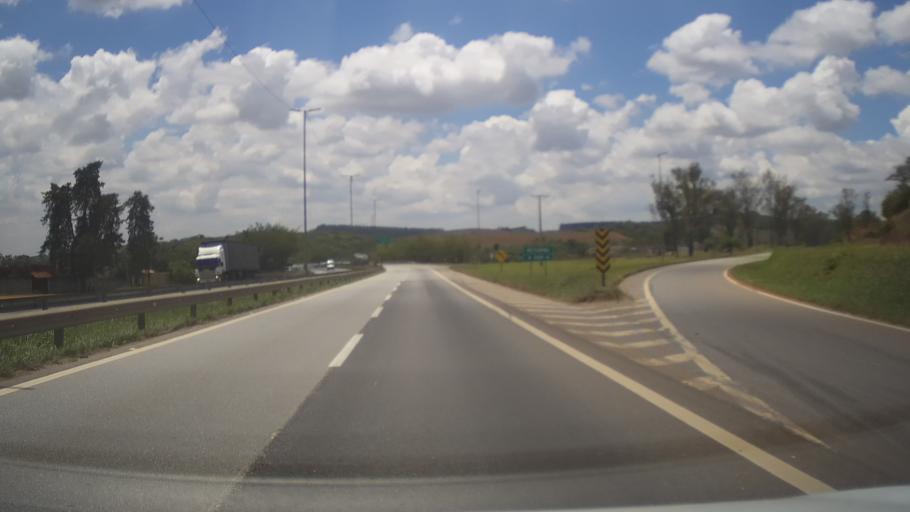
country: BR
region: Minas Gerais
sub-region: Campanha
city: Campanha
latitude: -21.7885
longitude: -45.4401
